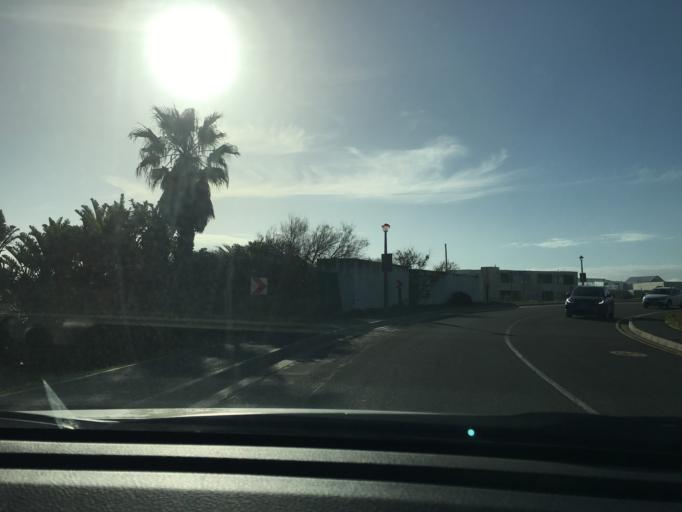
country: ZA
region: Western Cape
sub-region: City of Cape Town
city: Sunset Beach
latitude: -33.7946
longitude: 18.4588
